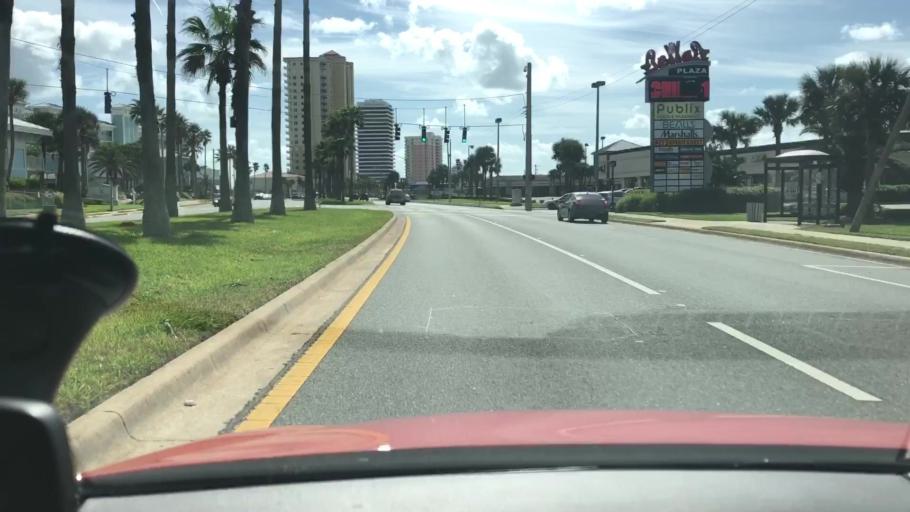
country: US
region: Florida
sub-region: Volusia County
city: Holly Hill
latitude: 29.2626
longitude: -81.0259
